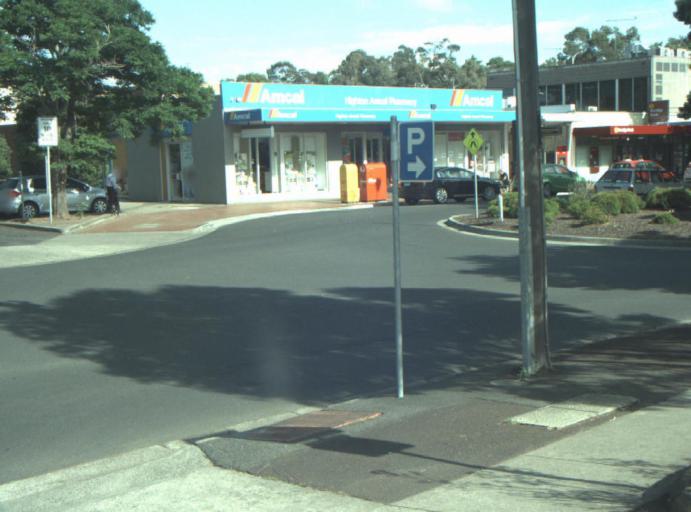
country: AU
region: Victoria
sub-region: Greater Geelong
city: Wandana Heights
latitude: -38.1729
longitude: 144.3243
